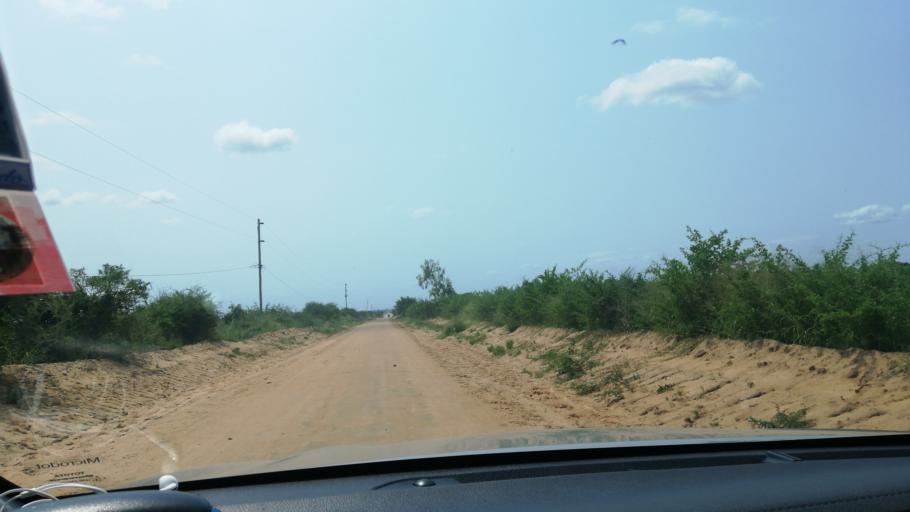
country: MZ
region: Maputo
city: Matola
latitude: -26.0965
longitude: 32.3892
